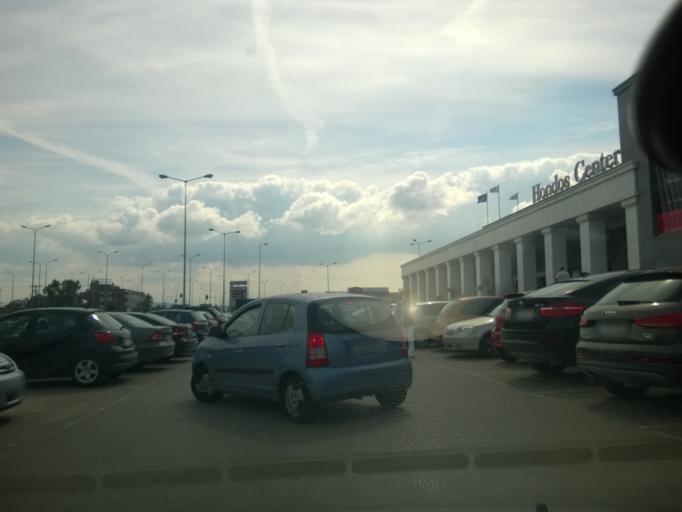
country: GR
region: Central Macedonia
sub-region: Nomos Thessalonikis
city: Thermi
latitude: 40.5487
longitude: 22.9828
